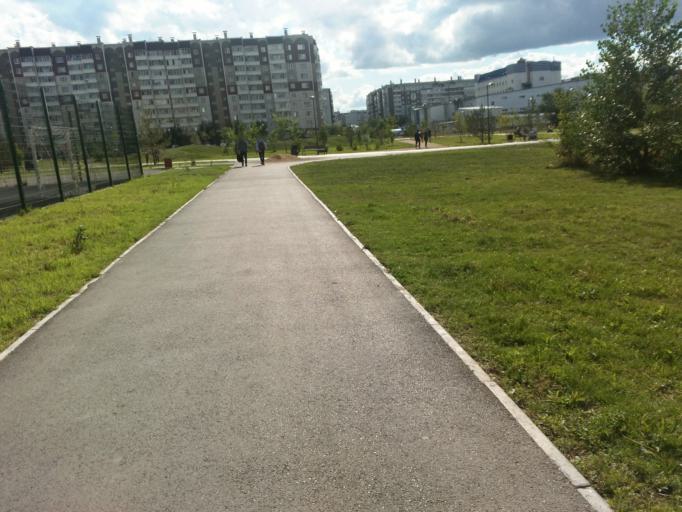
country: RU
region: Krasnoyarskiy
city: Krasnoyarsk
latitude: 56.0427
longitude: 92.9175
